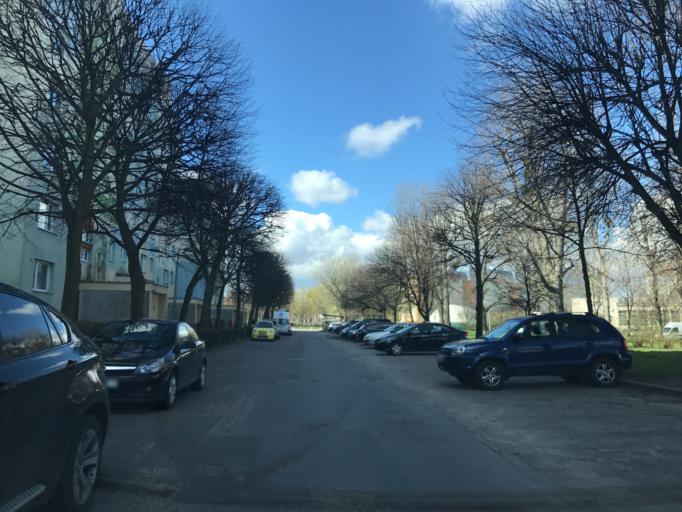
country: PL
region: Pomeranian Voivodeship
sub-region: Gdansk
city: Gdansk
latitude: 54.3950
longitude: 18.6126
